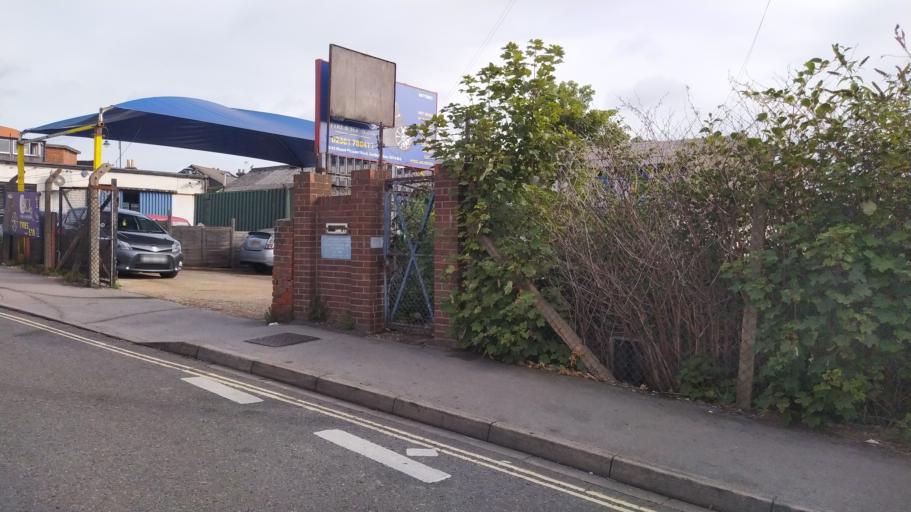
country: GB
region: England
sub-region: Southampton
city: Southampton
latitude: 50.9157
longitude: -1.3958
